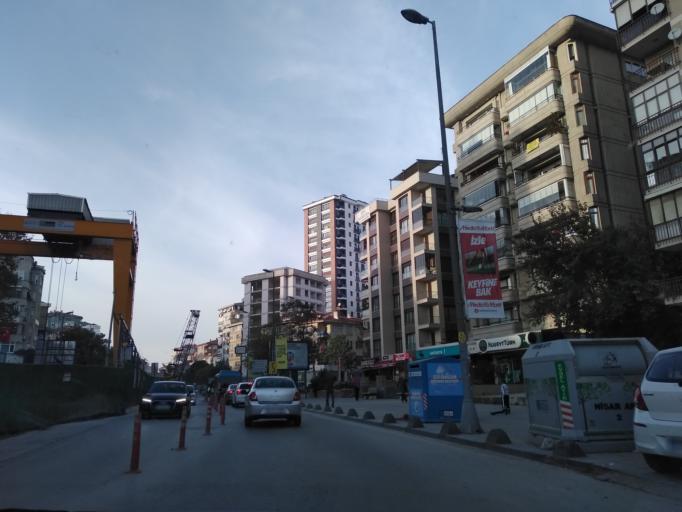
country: TR
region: Istanbul
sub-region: Atasehir
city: Atasehir
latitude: 40.9659
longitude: 29.0874
